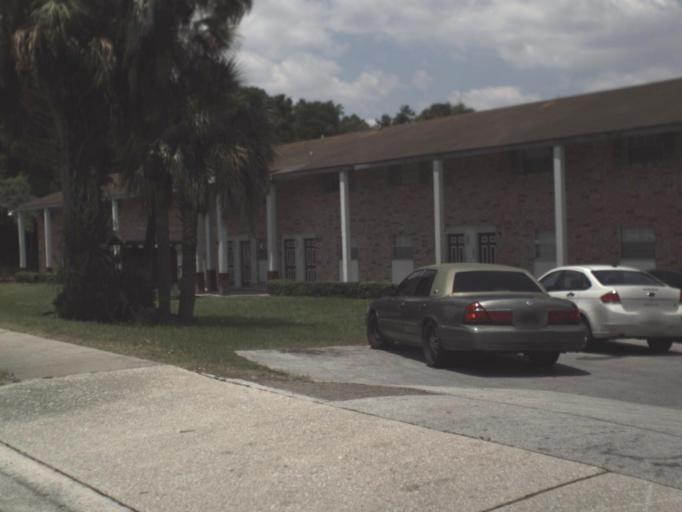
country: US
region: Florida
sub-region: Duval County
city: Jacksonville
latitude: 30.3849
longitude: -81.6899
